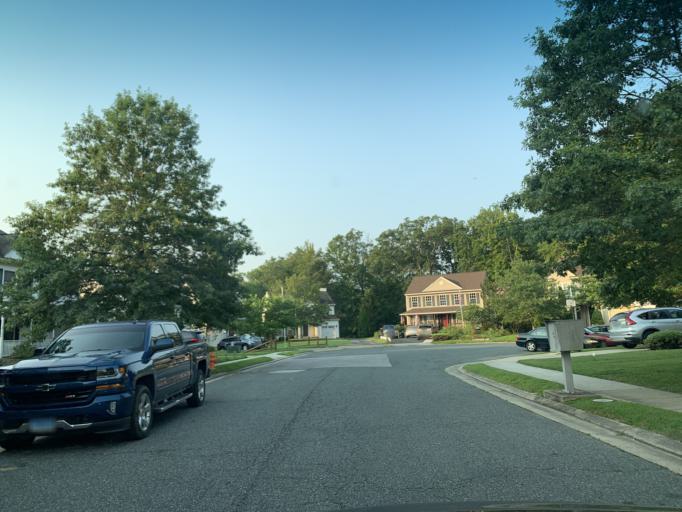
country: US
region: Maryland
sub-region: Baltimore County
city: Bowleys Quarters
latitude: 39.3664
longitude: -76.3666
